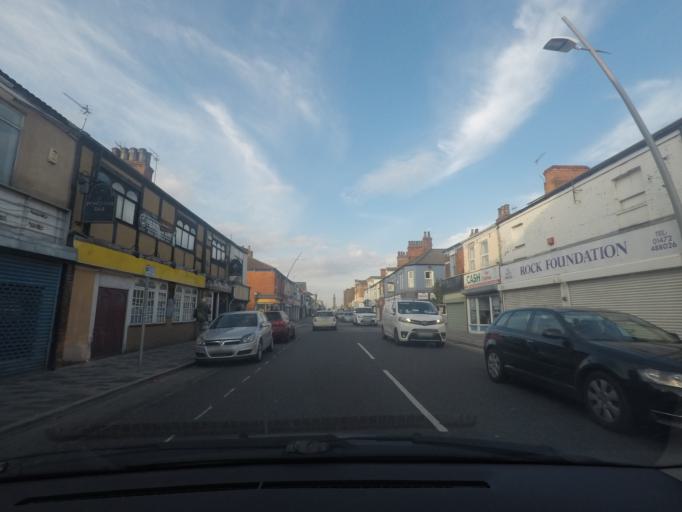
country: GB
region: England
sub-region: North East Lincolnshire
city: Grimsby
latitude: 53.5691
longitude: -0.0743
